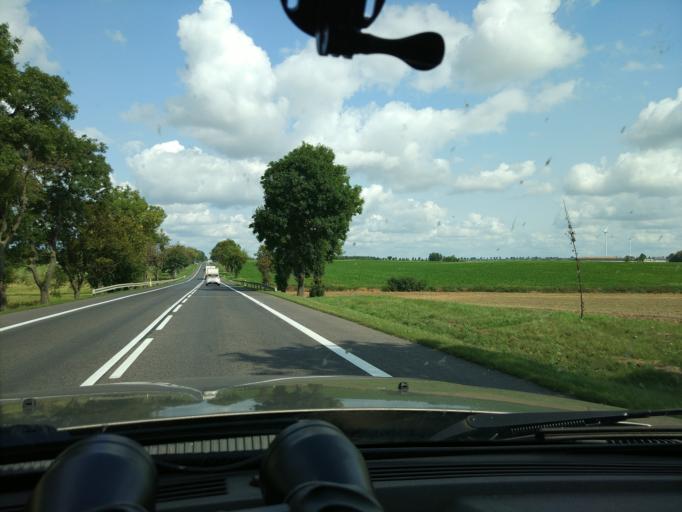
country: PL
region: Masovian Voivodeship
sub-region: Powiat mlawski
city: Wisniewo
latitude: 53.0450
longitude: 20.3421
